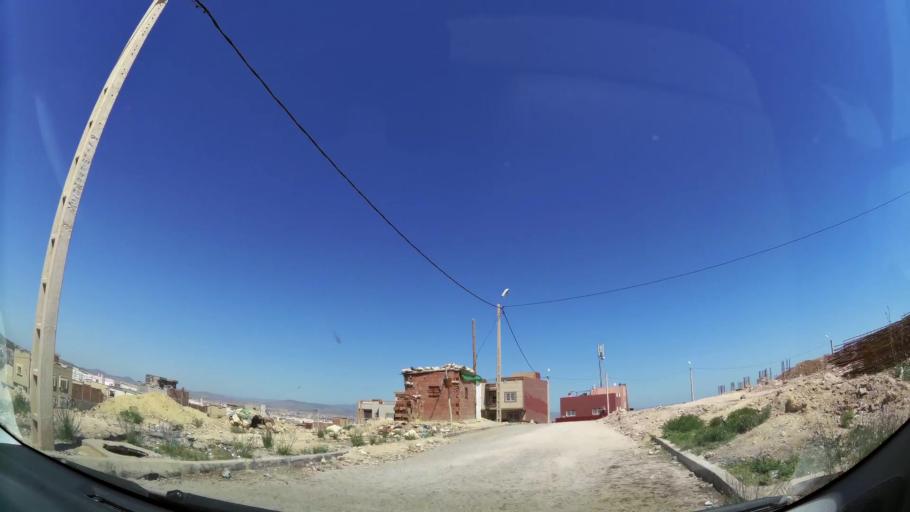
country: MA
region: Oriental
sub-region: Oujda-Angad
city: Oujda
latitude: 34.6517
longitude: -1.8706
